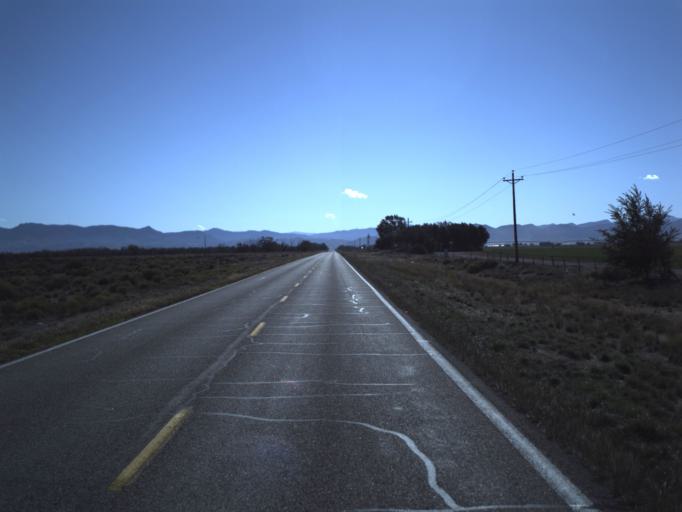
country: US
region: Utah
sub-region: Washington County
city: Enterprise
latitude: 37.7223
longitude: -113.6919
